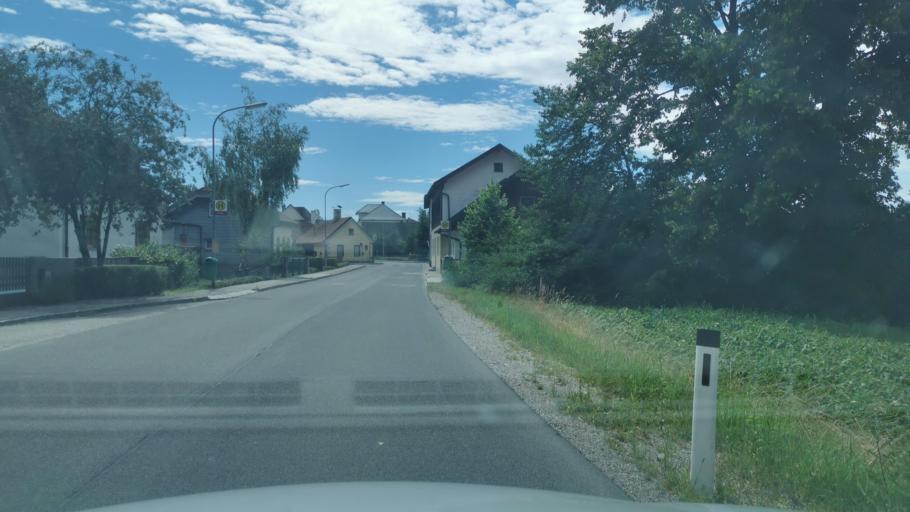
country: AT
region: Lower Austria
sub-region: Politischer Bezirk Sankt Polten
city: Wilhelmsburg
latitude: 48.1342
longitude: 15.6378
